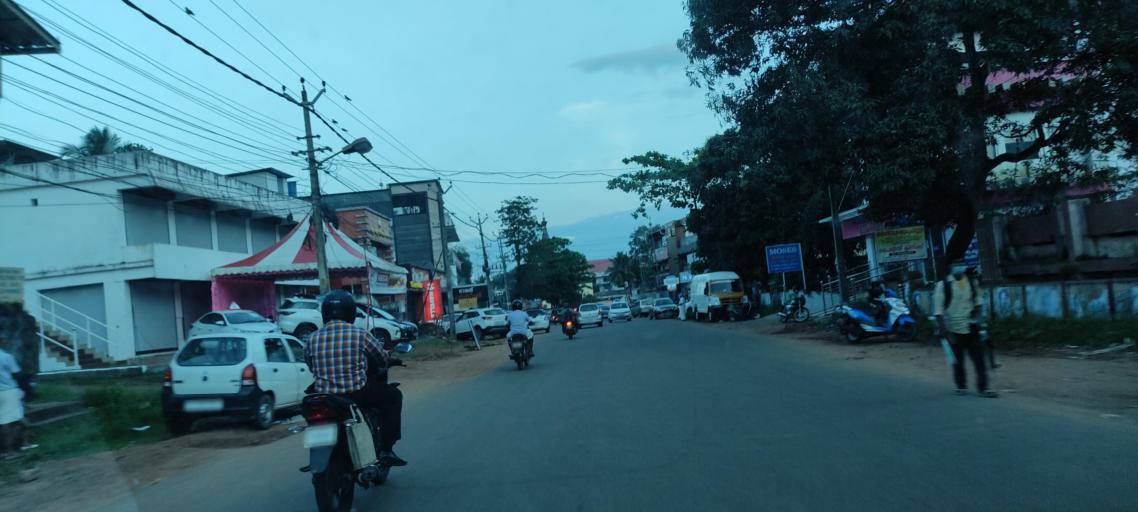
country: IN
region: Kerala
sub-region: Pattanamtitta
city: Adur
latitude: 9.1589
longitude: 76.7251
